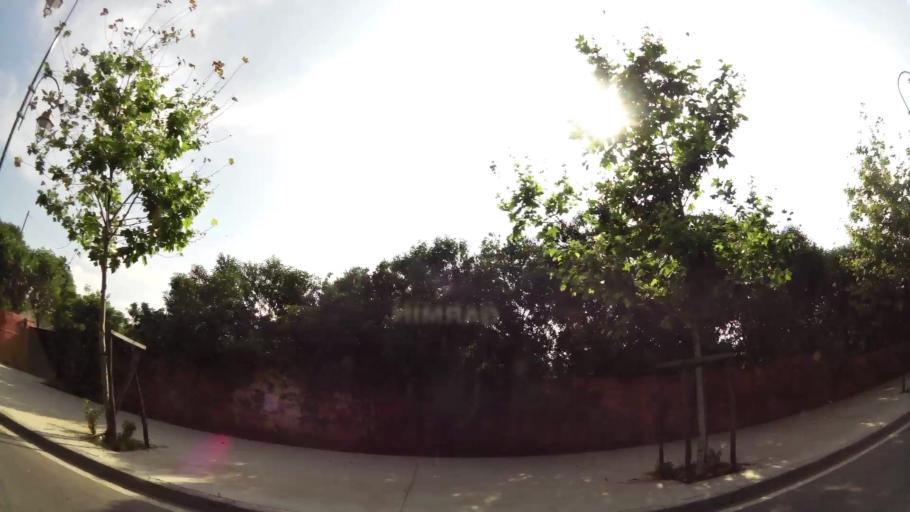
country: MA
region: Rabat-Sale-Zemmour-Zaer
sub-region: Rabat
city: Rabat
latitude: 33.9577
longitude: -6.8181
